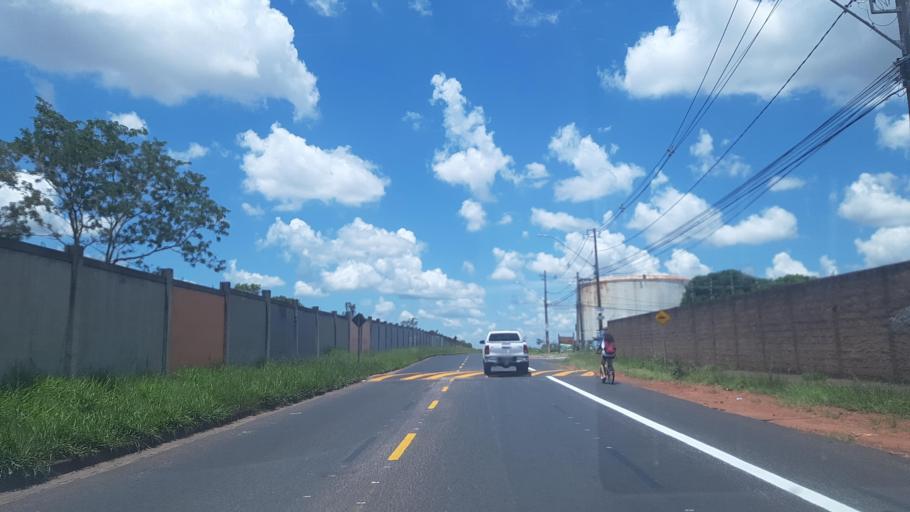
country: BR
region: Minas Gerais
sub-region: Uberlandia
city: Uberlandia
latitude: -18.9595
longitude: -48.3361
